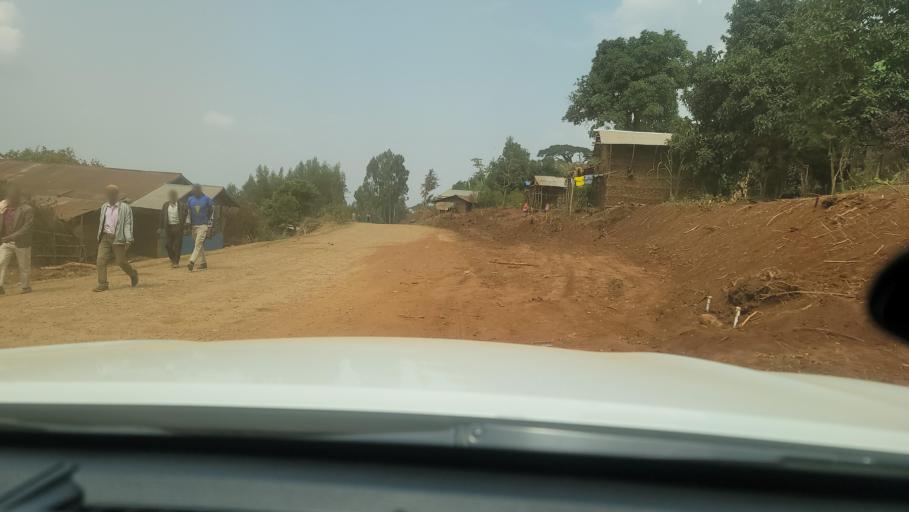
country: ET
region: Oromiya
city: Agaro
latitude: 7.8048
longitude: 36.4607
